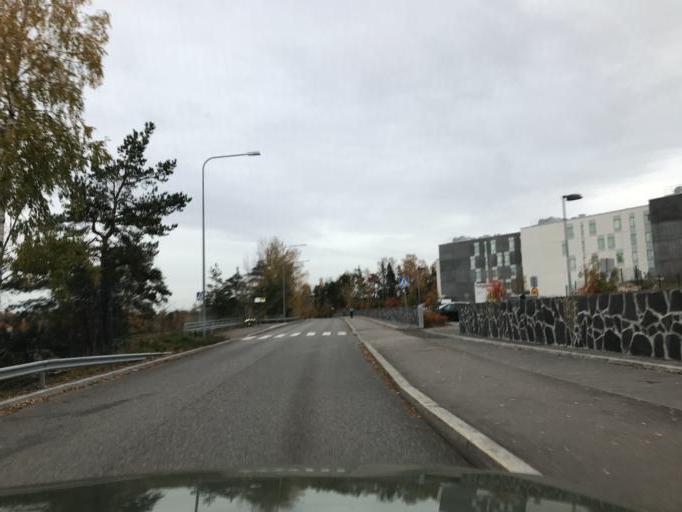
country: FI
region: Uusimaa
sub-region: Helsinki
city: Vantaa
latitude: 60.2588
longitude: 25.0713
